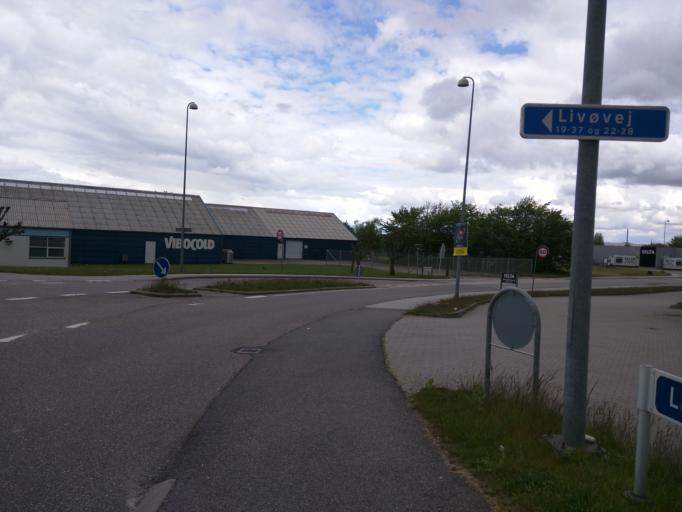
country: DK
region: Central Jutland
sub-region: Viborg Kommune
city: Viborg
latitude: 56.4486
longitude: 9.3662
